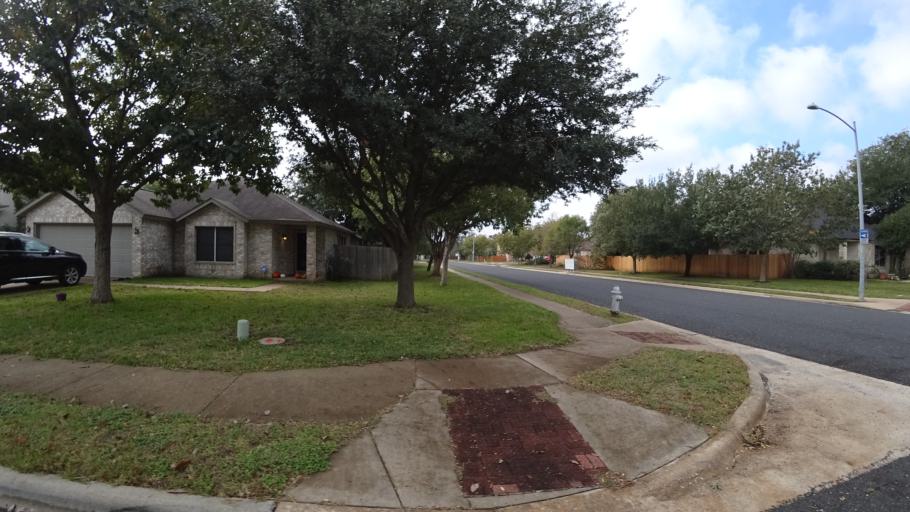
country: US
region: Texas
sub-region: Travis County
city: Shady Hollow
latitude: 30.2147
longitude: -97.8427
